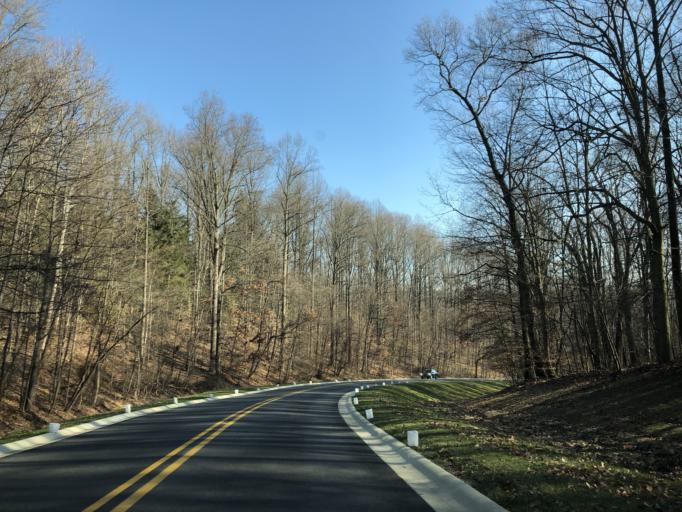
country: US
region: Pennsylvania
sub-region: Chester County
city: Downingtown
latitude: 39.9896
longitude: -75.6993
